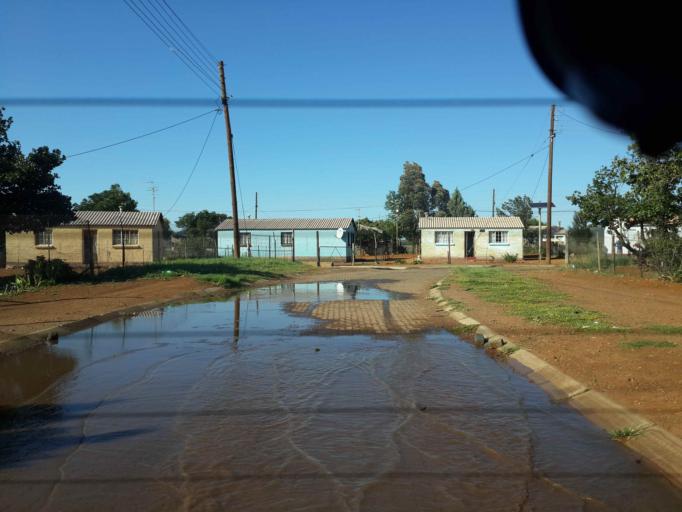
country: ZA
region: Northern Cape
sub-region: Siyanda District Municipality
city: Danielskuil
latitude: -28.1968
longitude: 23.5322
